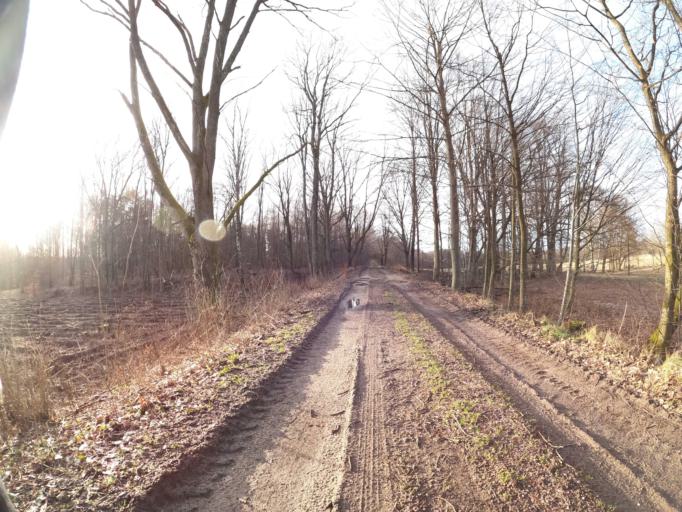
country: PL
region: West Pomeranian Voivodeship
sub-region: Powiat koszalinski
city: Polanow
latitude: 54.1757
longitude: 16.7385
